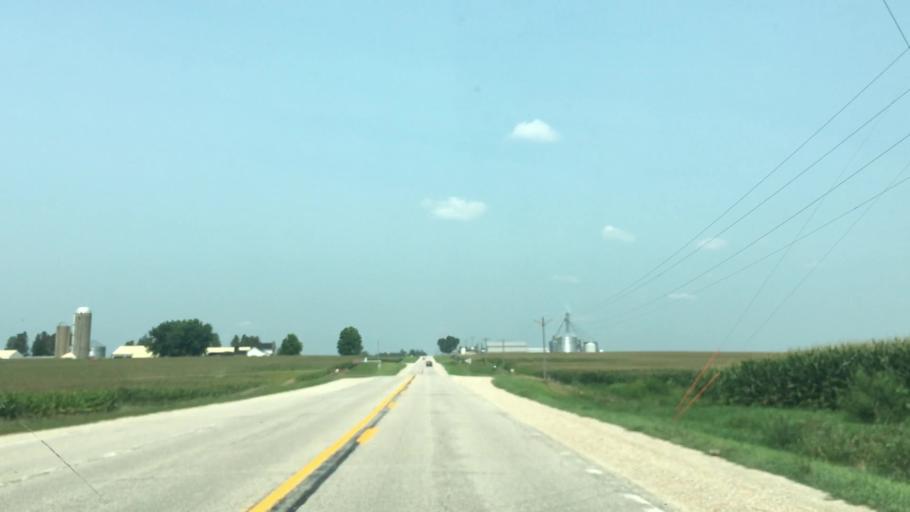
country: US
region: Iowa
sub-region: Benton County
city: Urbana
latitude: 42.3134
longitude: -91.8894
